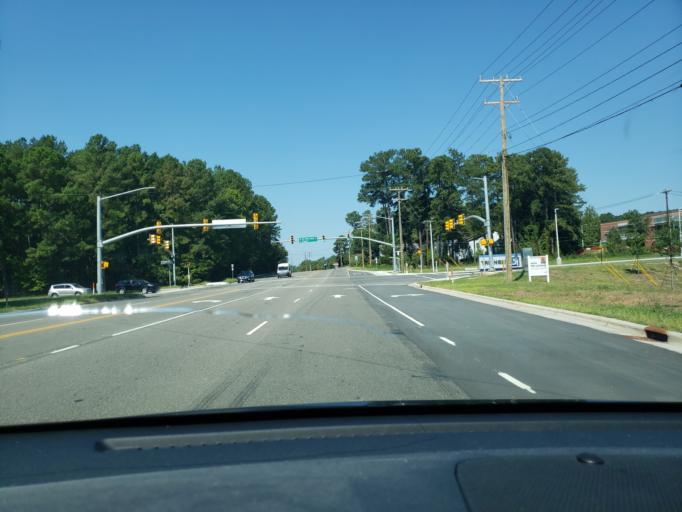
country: US
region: North Carolina
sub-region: Durham County
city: Durham
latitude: 35.9000
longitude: -78.8837
